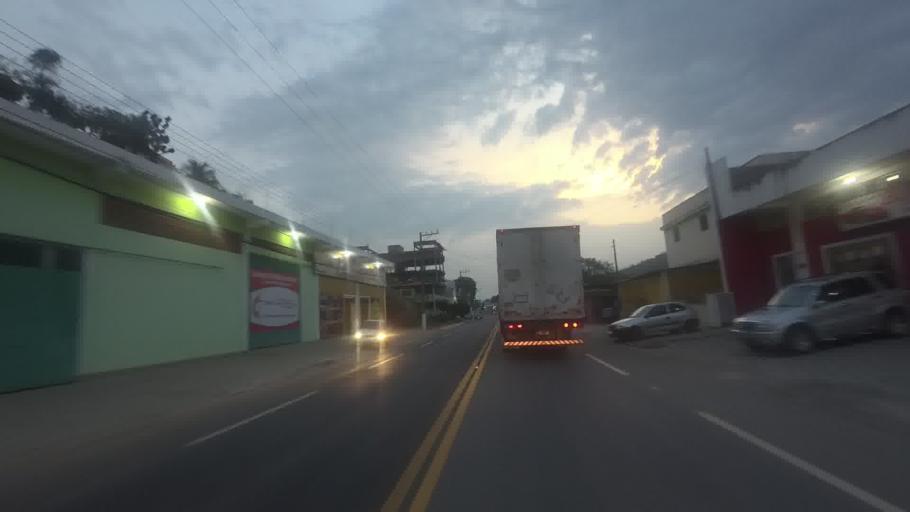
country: BR
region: Minas Gerais
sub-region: Alem Paraiba
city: Alem Paraiba
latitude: -21.8897
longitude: -42.7042
